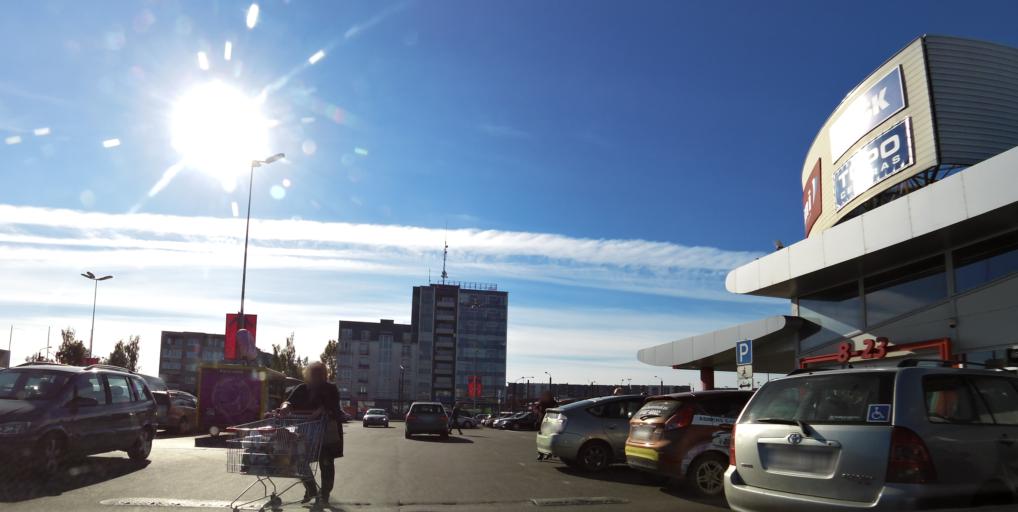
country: LT
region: Vilnius County
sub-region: Vilnius
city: Vilnius
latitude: 54.7122
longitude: 25.3034
